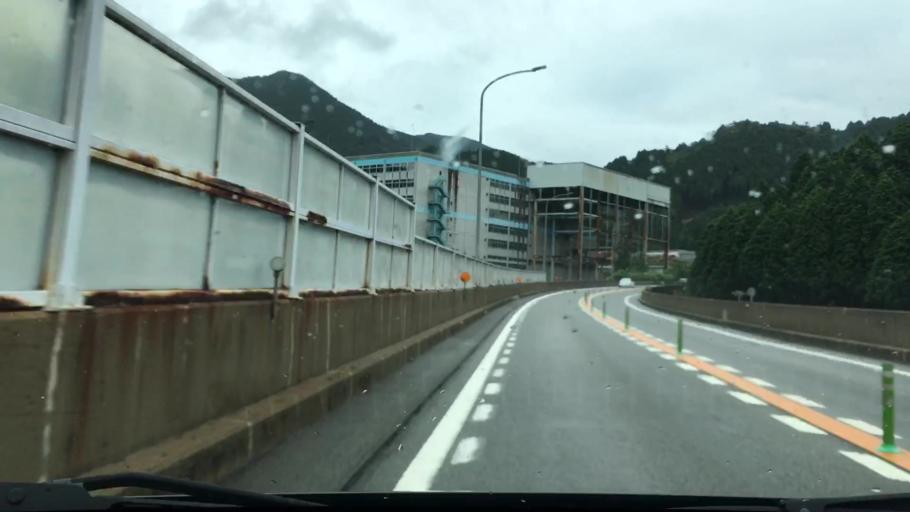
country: JP
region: Hyogo
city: Nishiwaki
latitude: 35.1494
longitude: 134.7874
